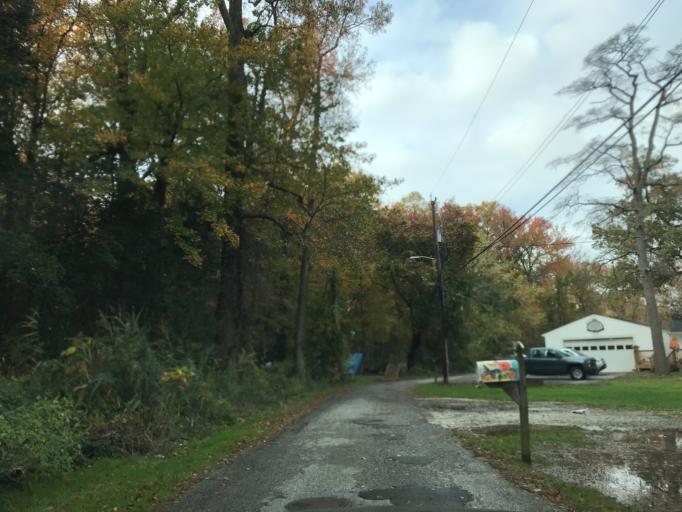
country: US
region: Maryland
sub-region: Baltimore County
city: Bowleys Quarters
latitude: 39.3228
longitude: -76.3869
